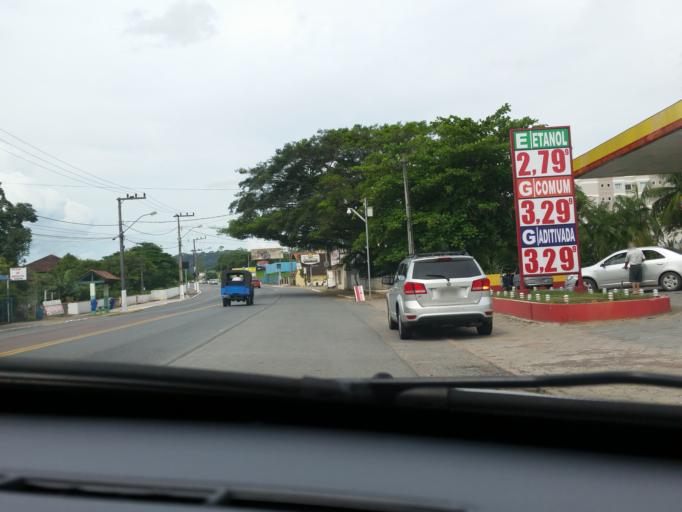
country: BR
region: Santa Catarina
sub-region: Rodeio
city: Gavea
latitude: -27.0321
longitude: -49.3849
